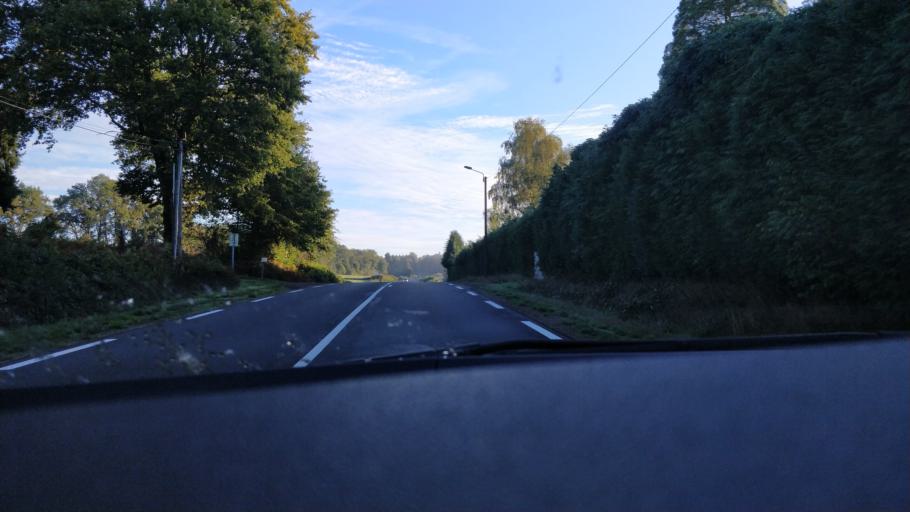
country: FR
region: Limousin
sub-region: Departement de la Haute-Vienne
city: Sauviat-sur-Vige
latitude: 45.9141
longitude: 1.6227
